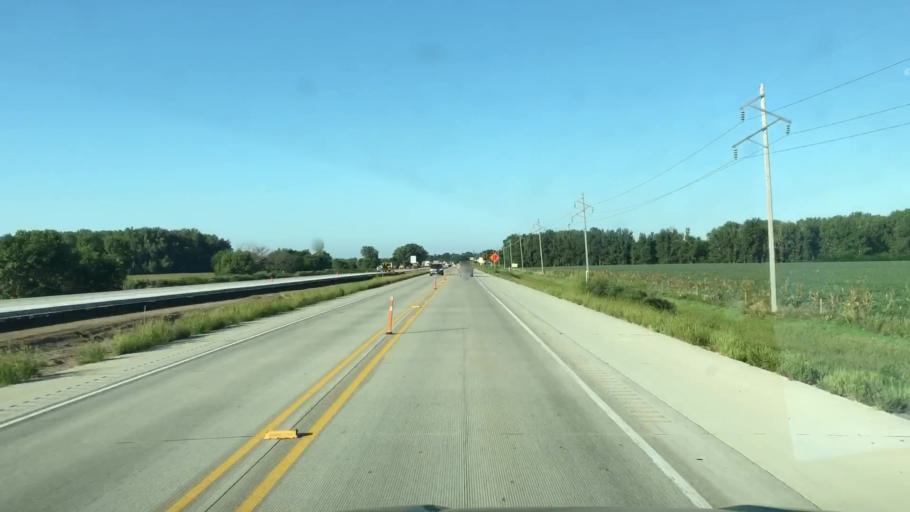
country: US
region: Iowa
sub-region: Plymouth County
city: Le Mars
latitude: 42.7285
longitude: -96.2347
